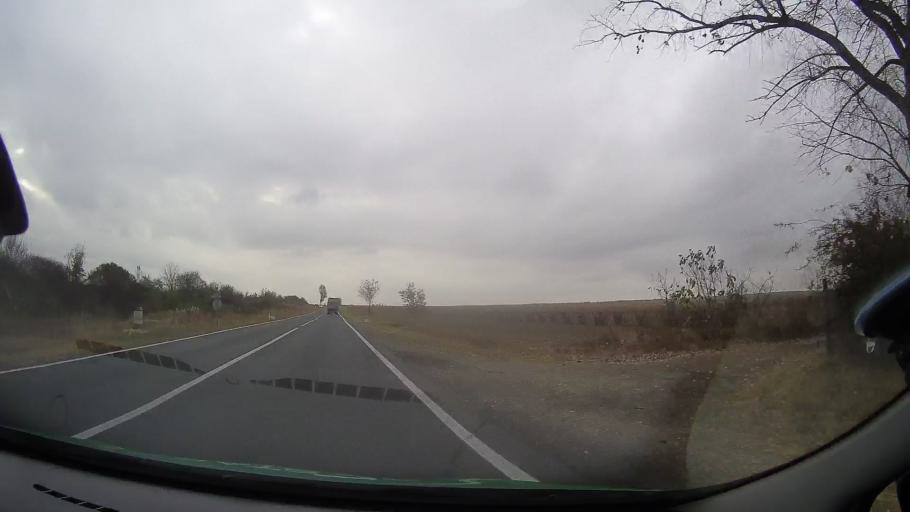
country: RO
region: Constanta
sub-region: Comuna Castelu
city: Castelu
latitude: 44.2533
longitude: 28.3215
